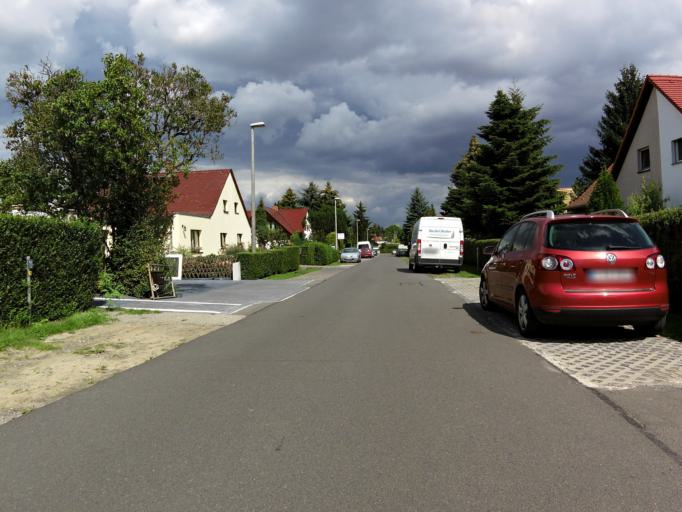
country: DE
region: Saxony
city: Leipzig
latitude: 51.3806
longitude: 12.4124
